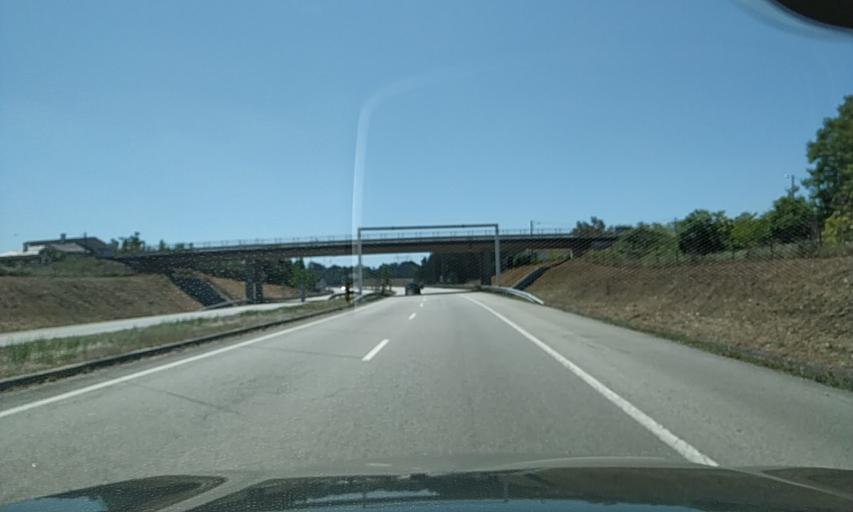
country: PT
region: Aveiro
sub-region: Agueda
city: Agueda
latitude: 40.5594
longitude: -8.4756
